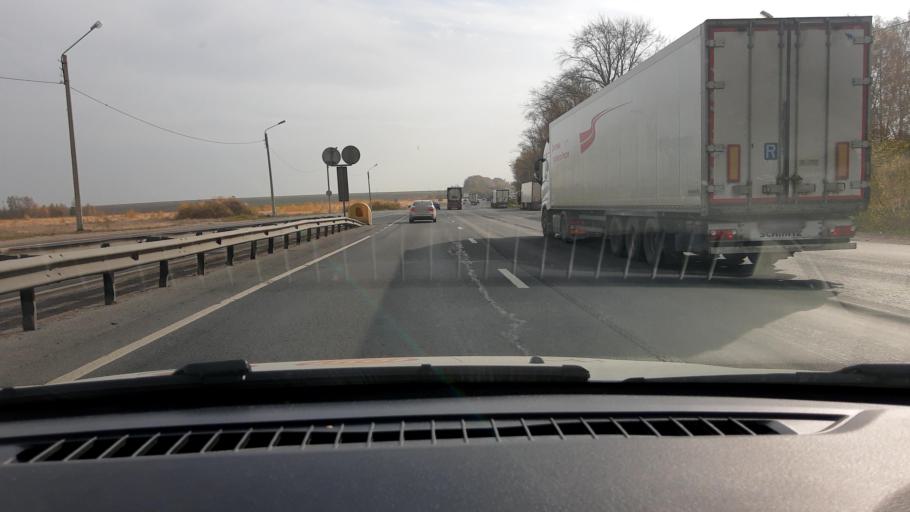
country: RU
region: Nizjnij Novgorod
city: Kstovo
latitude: 56.1240
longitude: 44.2679
